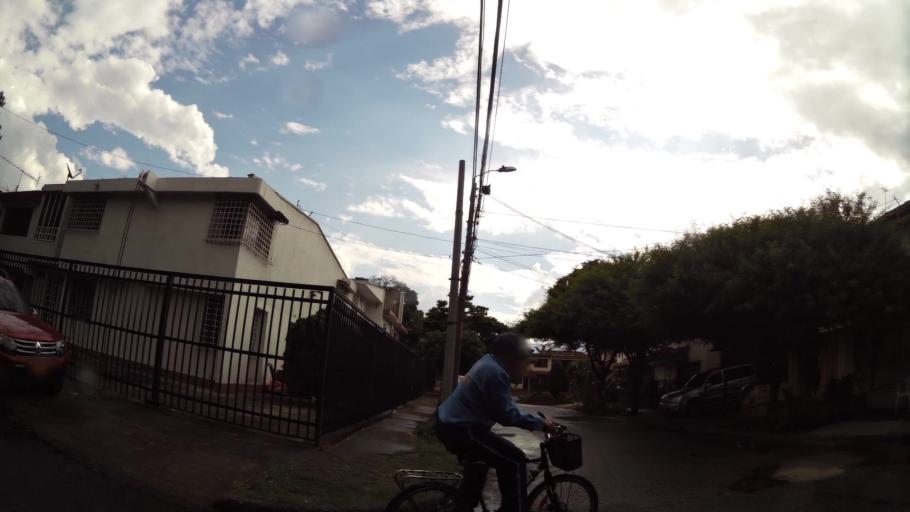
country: CO
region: Valle del Cauca
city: Cali
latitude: 3.4790
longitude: -76.5133
